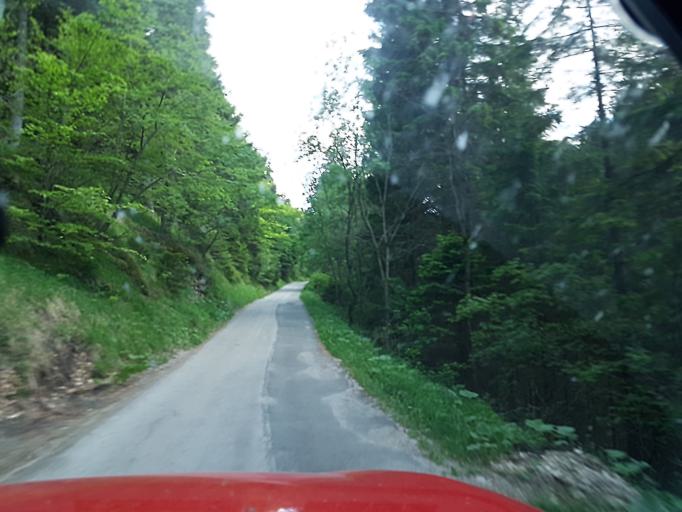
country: SK
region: Zilinsky
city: Ruzomberok
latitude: 49.0525
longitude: 19.2746
